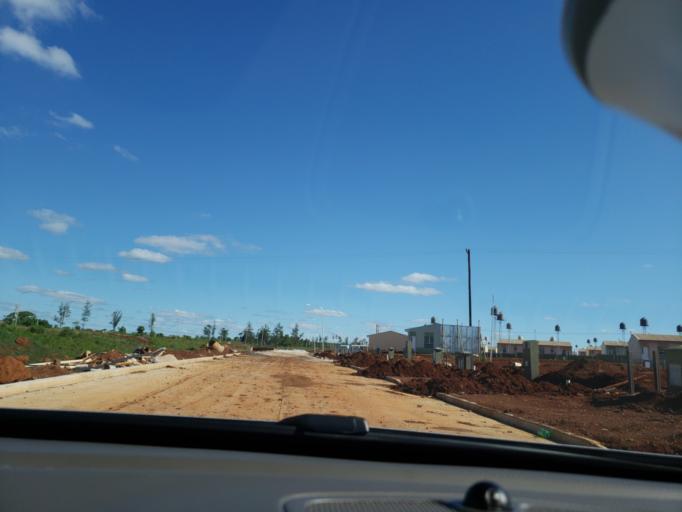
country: AR
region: Misiones
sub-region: Departamento de Capital
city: Posadas
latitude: -27.4122
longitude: -55.9893
